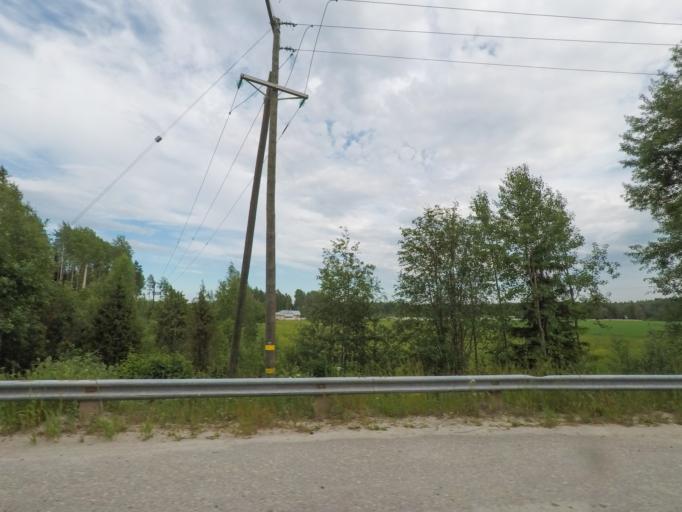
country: FI
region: Paijanne Tavastia
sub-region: Lahti
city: Lahti
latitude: 60.9290
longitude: 25.5829
